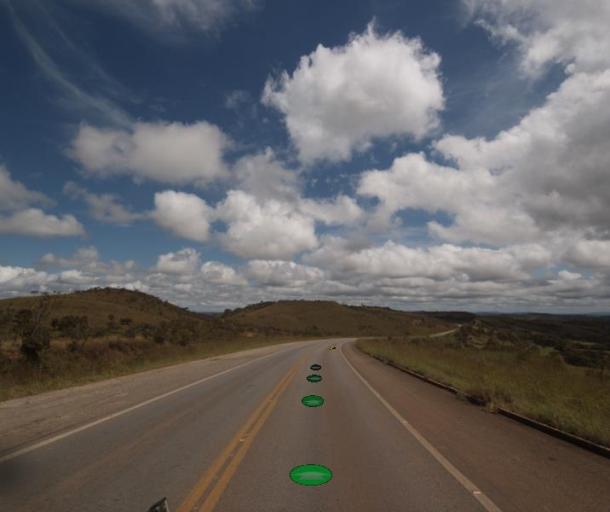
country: BR
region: Federal District
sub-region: Brasilia
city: Brasilia
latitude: -15.7536
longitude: -48.4156
